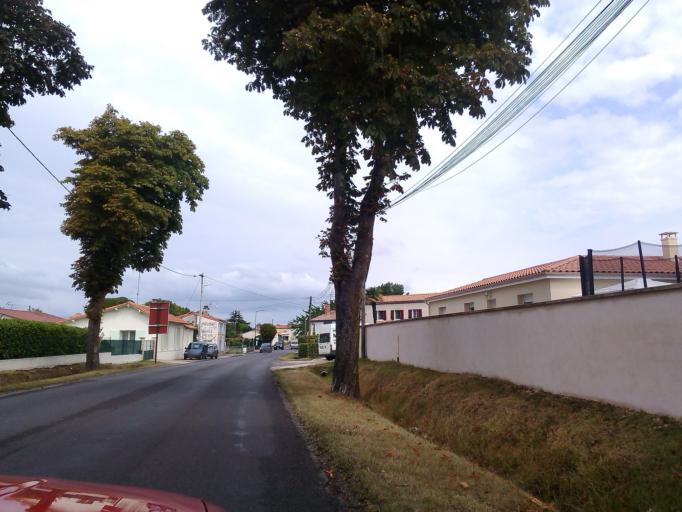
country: FR
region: Poitou-Charentes
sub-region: Departement de la Charente-Maritime
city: La Tremblade
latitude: 45.7603
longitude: -1.1414
